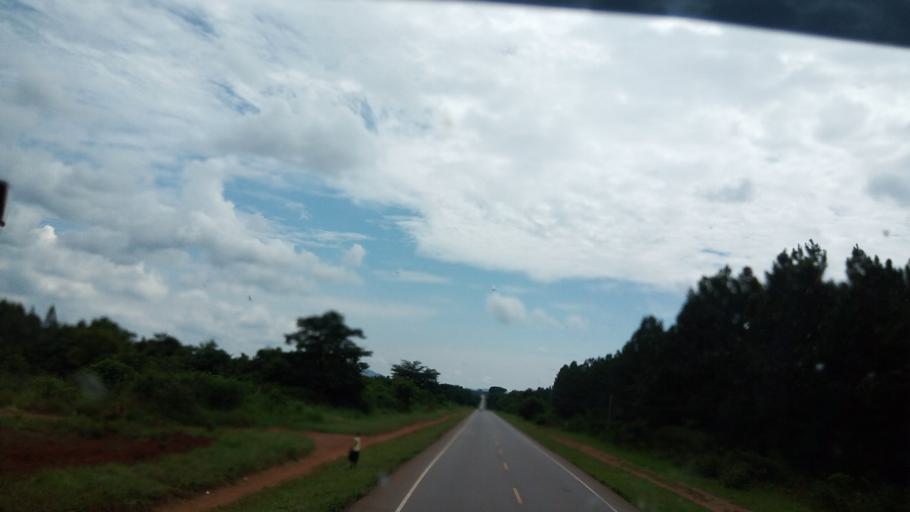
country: UG
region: Central Region
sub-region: Nakasongola District
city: Nakasongola
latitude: 1.1959
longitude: 32.4621
